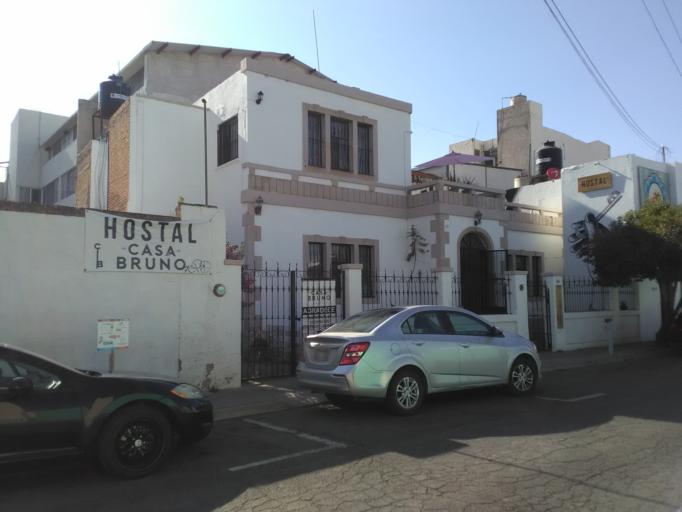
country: MX
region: Durango
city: Victoria de Durango
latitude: 24.0215
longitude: -104.6711
